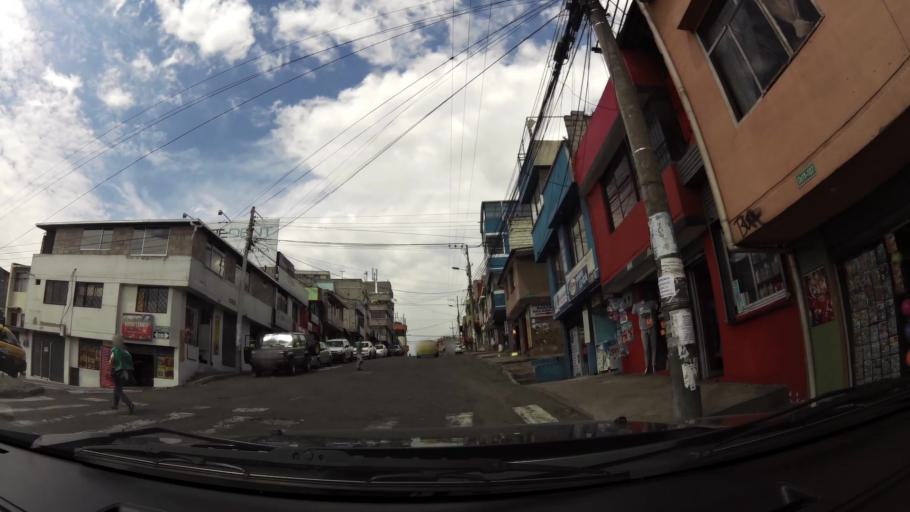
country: EC
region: Pichincha
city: Quito
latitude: -0.0924
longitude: -78.4505
